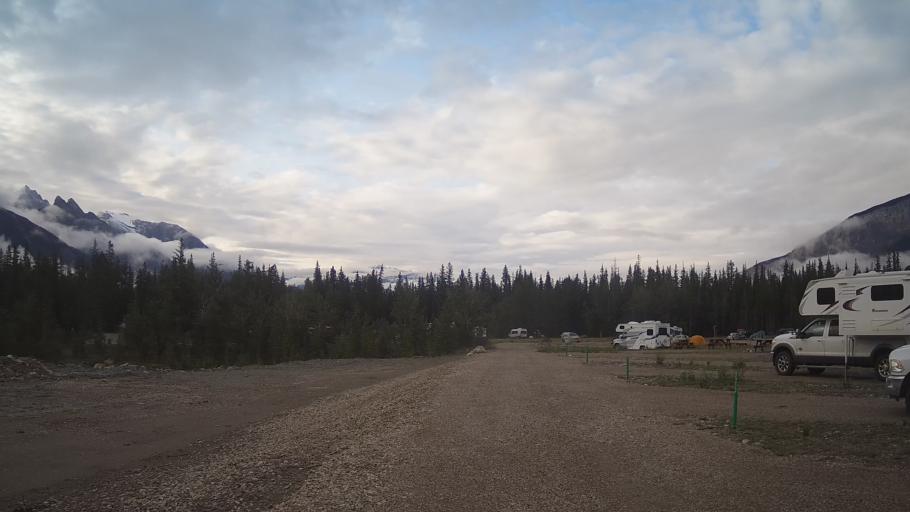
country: CA
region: Alberta
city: Jasper Park Lodge
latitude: 53.0167
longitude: -118.0839
